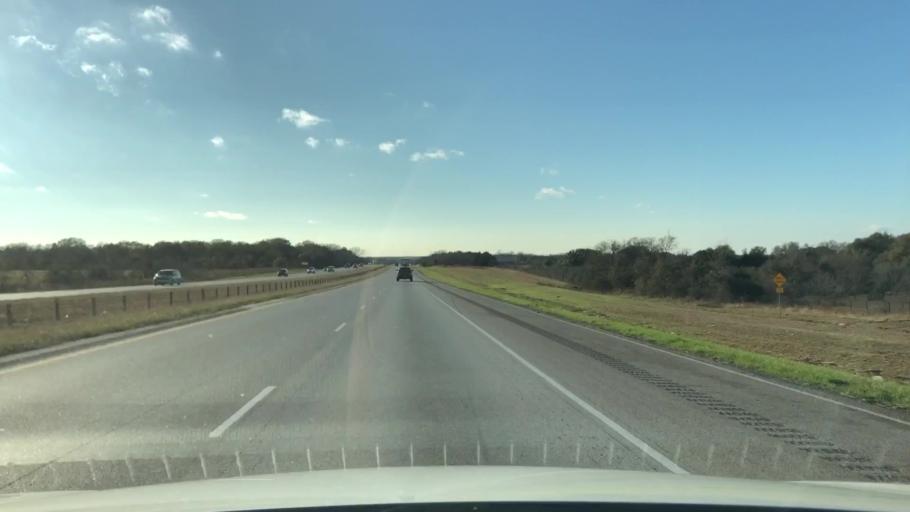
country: US
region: Texas
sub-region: Colorado County
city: Weimar
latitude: 29.6862
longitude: -96.8161
